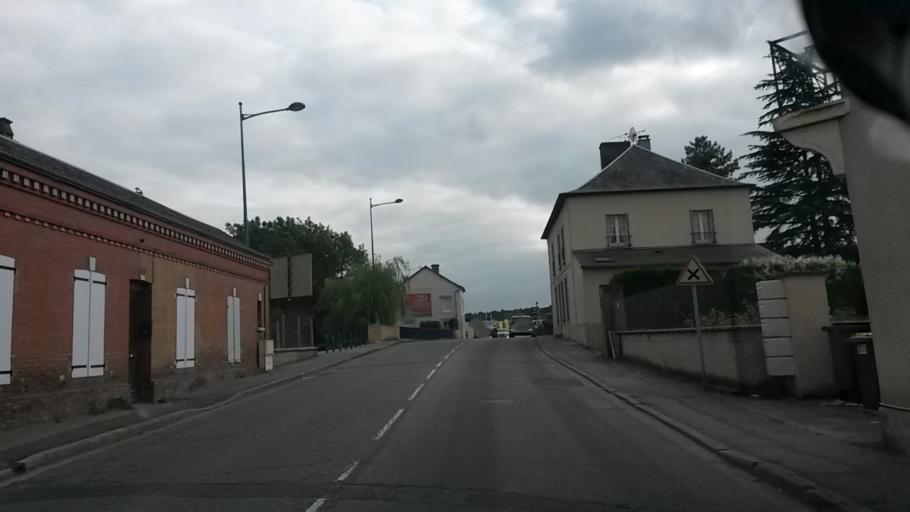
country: FR
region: Haute-Normandie
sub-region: Departement de l'Eure
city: Gravigny
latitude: 49.0468
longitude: 1.1624
